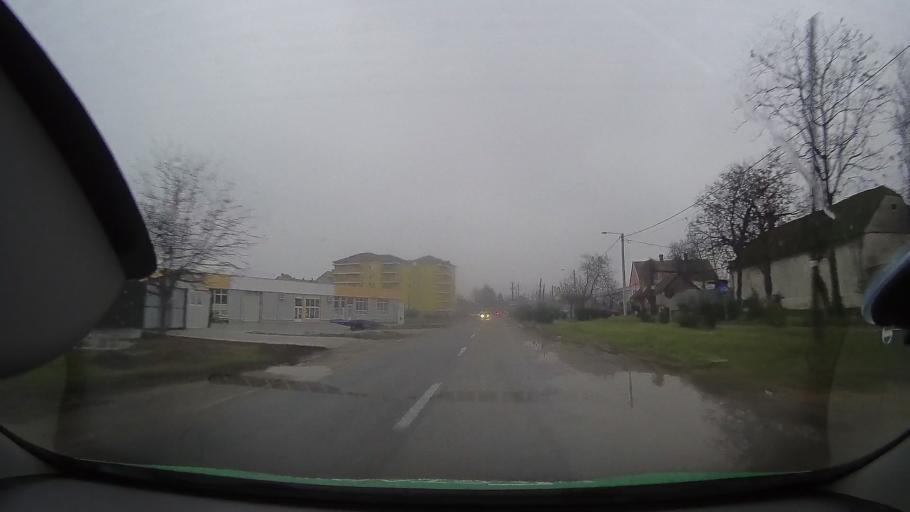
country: RO
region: Bihor
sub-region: Municipiul Salonta
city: Salonta
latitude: 46.8034
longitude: 21.6442
